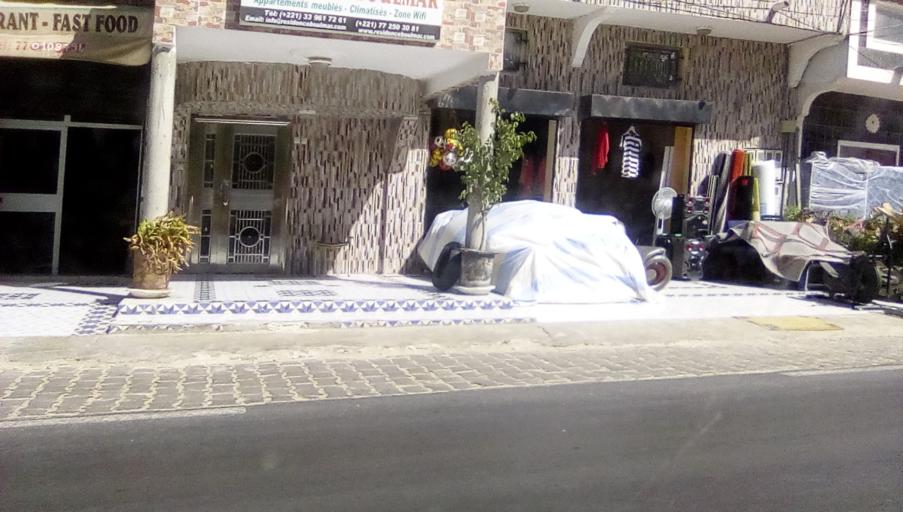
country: SN
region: Saint-Louis
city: Saint-Louis
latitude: 16.0355
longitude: -16.4688
